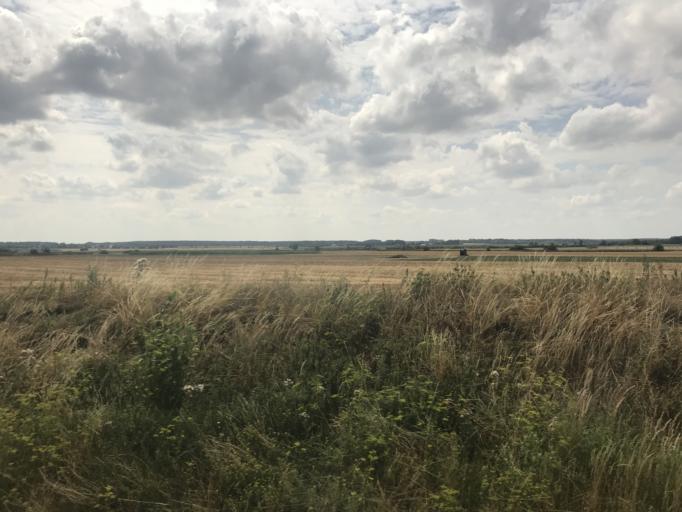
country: PL
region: Greater Poland Voivodeship
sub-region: Powiat poznanski
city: Pobiedziska
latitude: 52.4878
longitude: 17.3373
